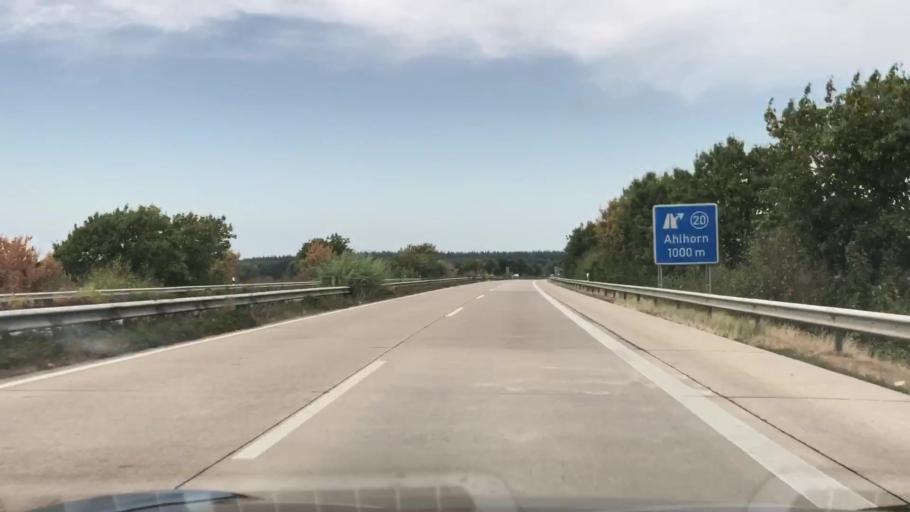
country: DE
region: Lower Saxony
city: Emstek
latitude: 52.8868
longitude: 8.1824
